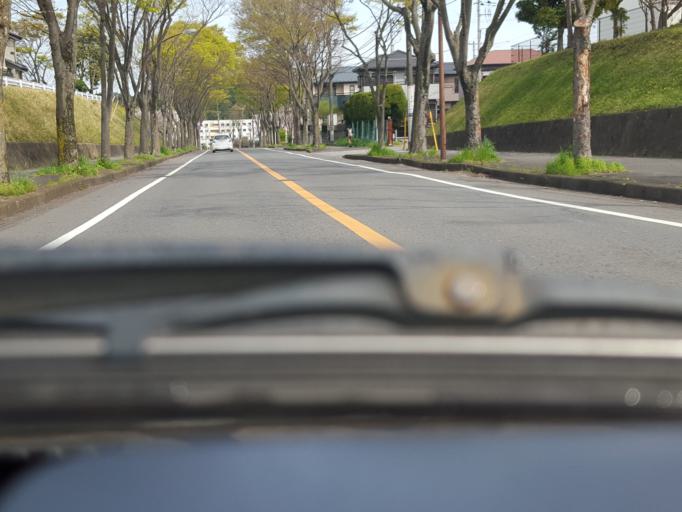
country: JP
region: Chiba
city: Ichihara
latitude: 35.4527
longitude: 140.0523
